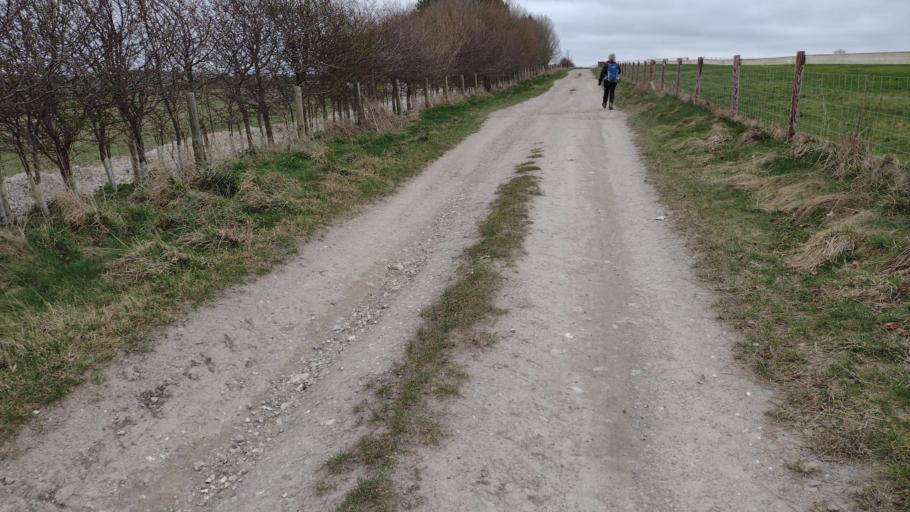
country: GB
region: England
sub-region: Wiltshire
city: Marlborough
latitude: 51.4550
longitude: -1.7575
